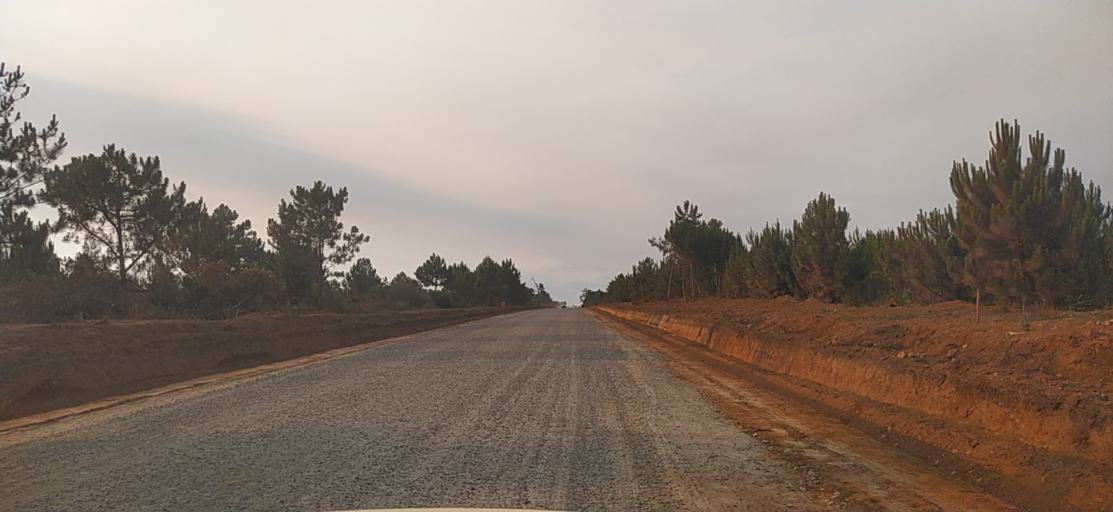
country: MG
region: Alaotra Mangoro
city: Moramanga
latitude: -18.5448
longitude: 48.2601
